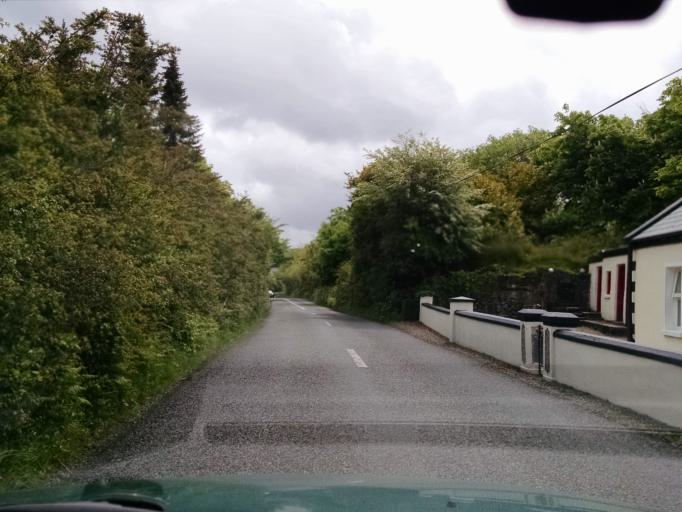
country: IE
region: Connaught
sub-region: County Galway
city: Bearna
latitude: 53.1267
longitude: -9.1810
